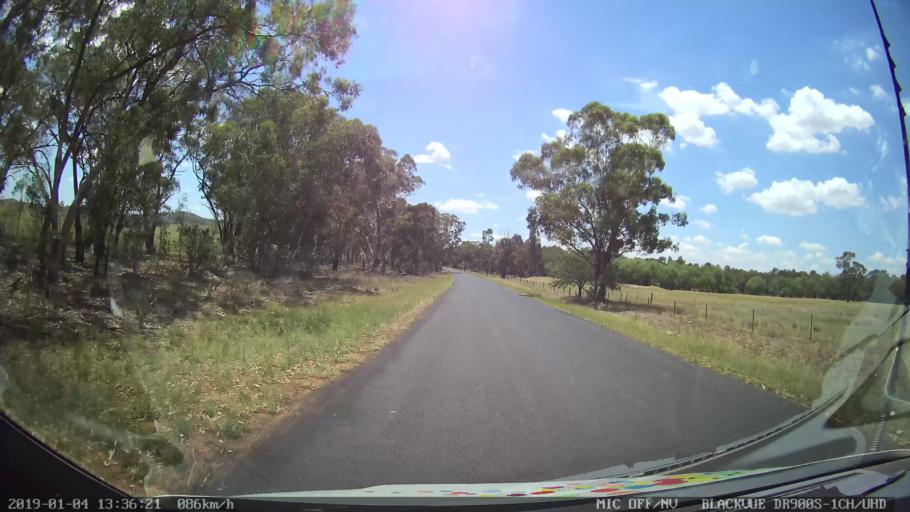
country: AU
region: New South Wales
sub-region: Dubbo Municipality
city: Dubbo
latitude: -32.5619
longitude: 148.5373
